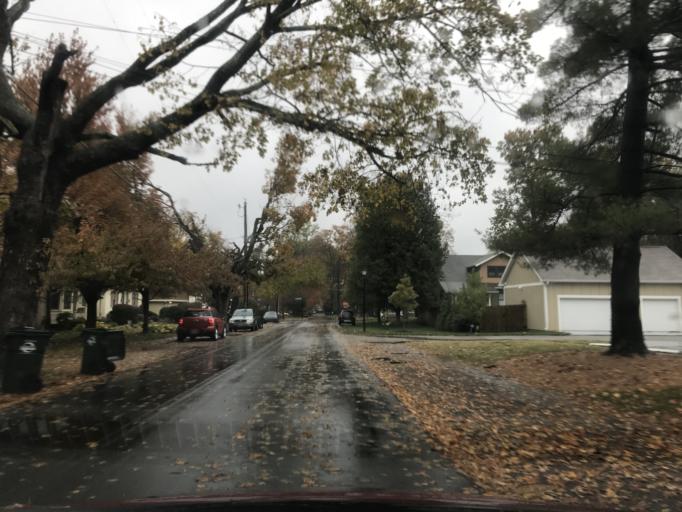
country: US
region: Kentucky
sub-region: Jefferson County
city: Saint Matthews
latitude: 38.2507
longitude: -85.6499
